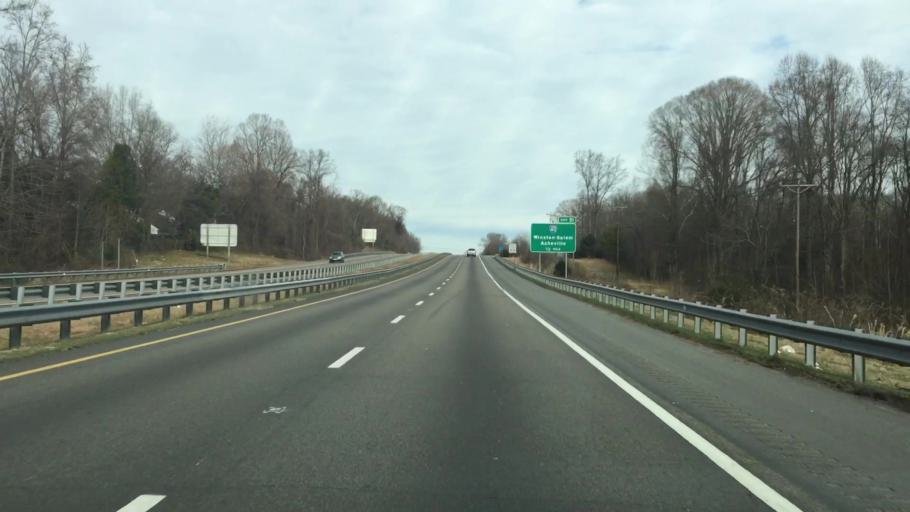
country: US
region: North Carolina
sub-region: Iredell County
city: Statesville
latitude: 35.7963
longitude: -80.8620
